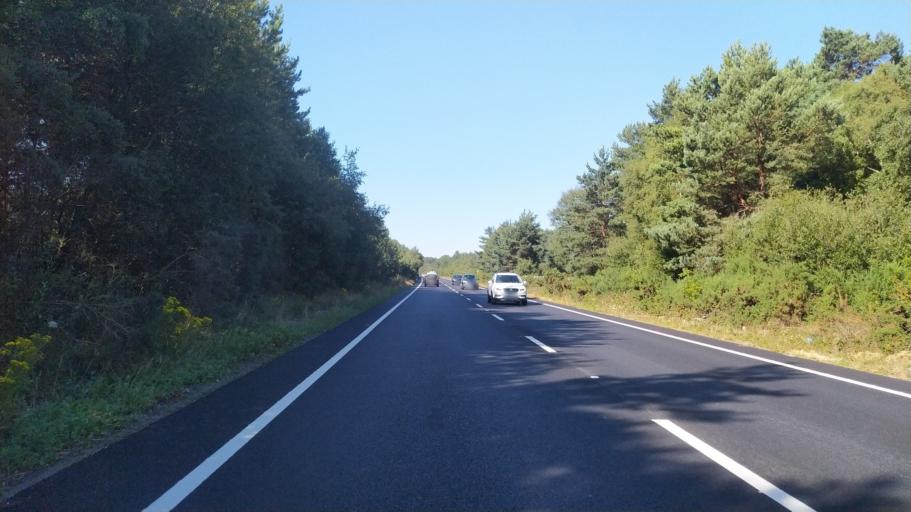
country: GB
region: England
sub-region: Dorset
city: Ferndown
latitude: 50.8132
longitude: -1.9217
